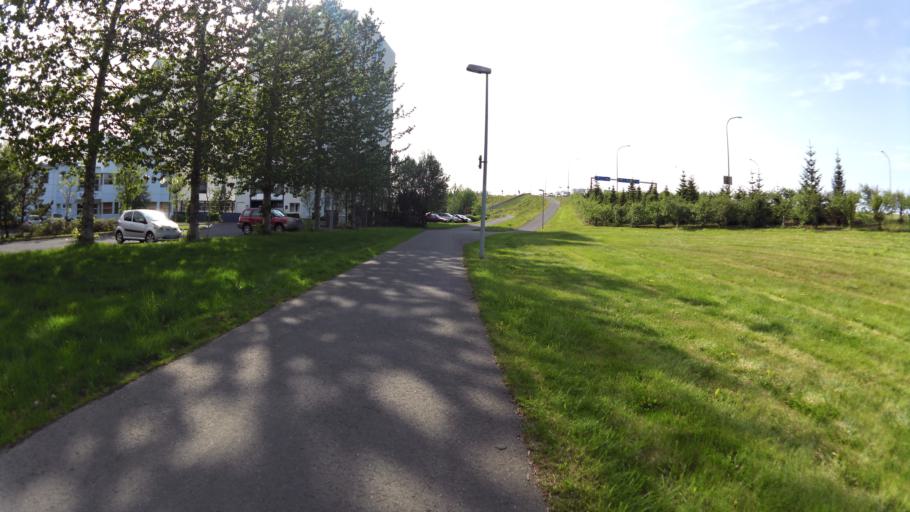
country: IS
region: Capital Region
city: Reykjavik
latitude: 64.1060
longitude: -21.8441
